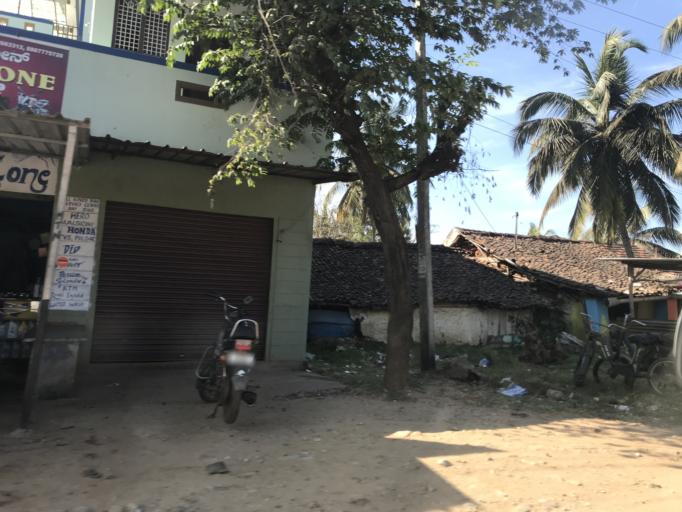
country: IN
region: Karnataka
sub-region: Mysore
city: Sargur
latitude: 12.1216
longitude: 76.4822
